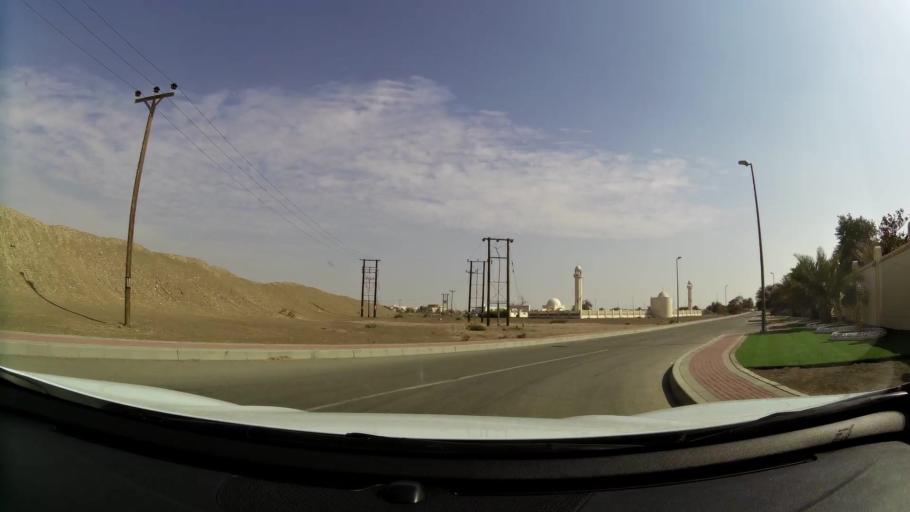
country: AE
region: Abu Dhabi
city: Al Ain
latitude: 24.0969
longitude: 55.9263
